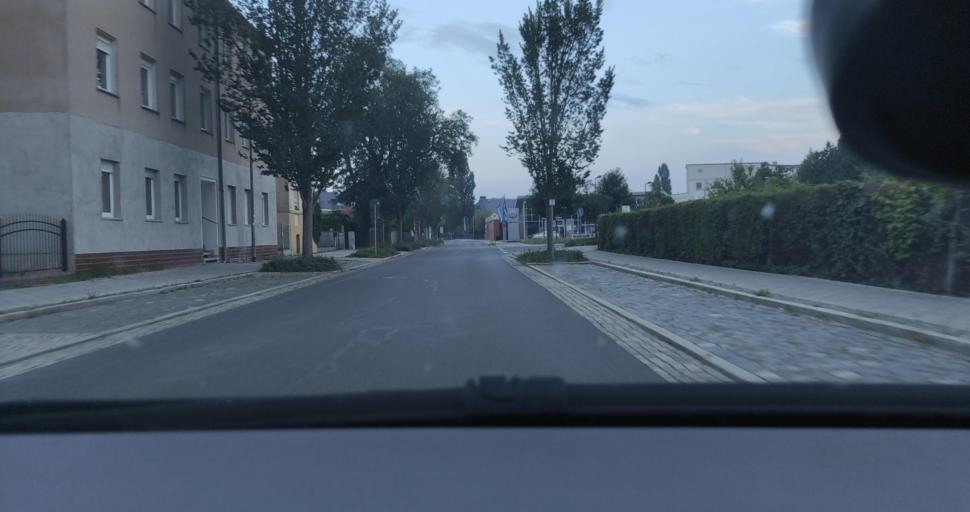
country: DE
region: Brandenburg
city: Forst
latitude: 51.7530
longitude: 14.6419
